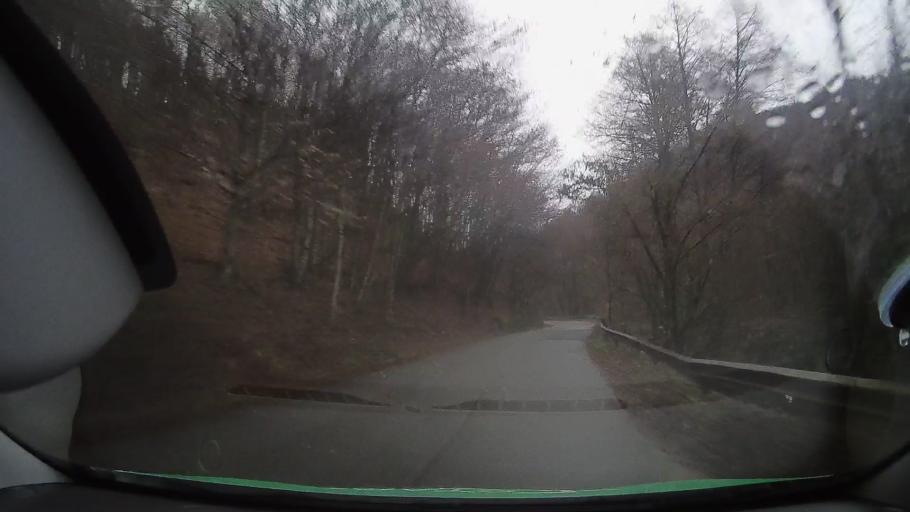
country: RO
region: Alba
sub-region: Comuna Avram Iancu
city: Avram Iancu
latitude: 46.2940
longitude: 22.7543
